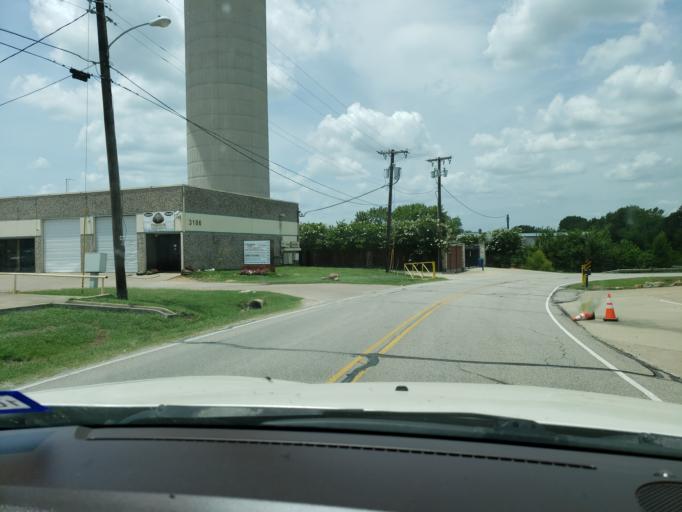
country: US
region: Texas
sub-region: Dallas County
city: Rowlett
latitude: 32.9023
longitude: -96.5721
